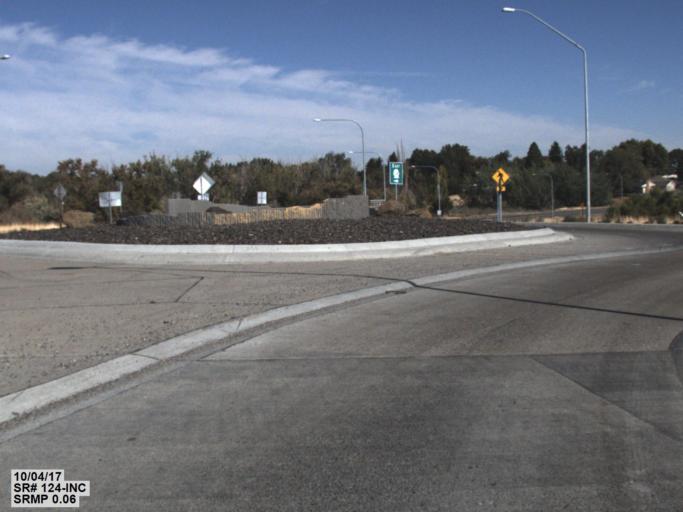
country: US
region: Washington
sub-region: Walla Walla County
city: Burbank
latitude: 46.2094
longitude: -119.0123
